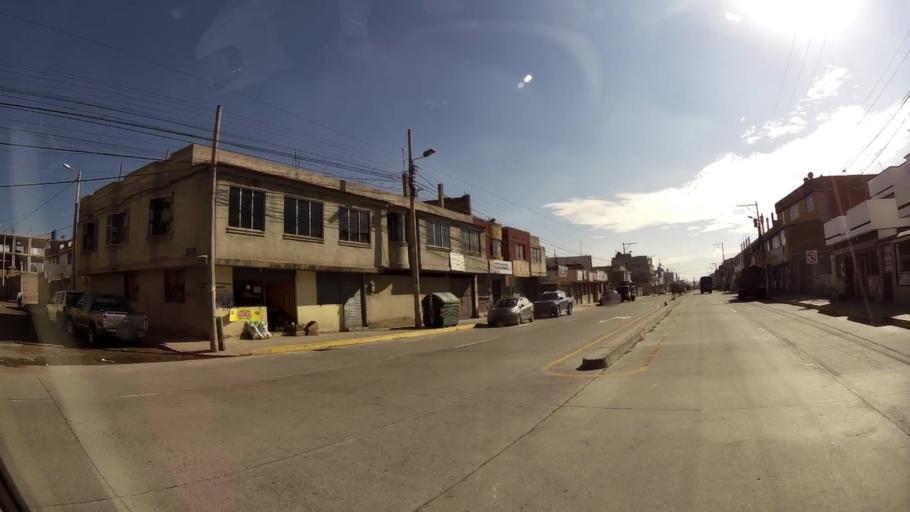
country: EC
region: Chimborazo
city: Riobamba
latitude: -1.6459
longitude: -78.6779
